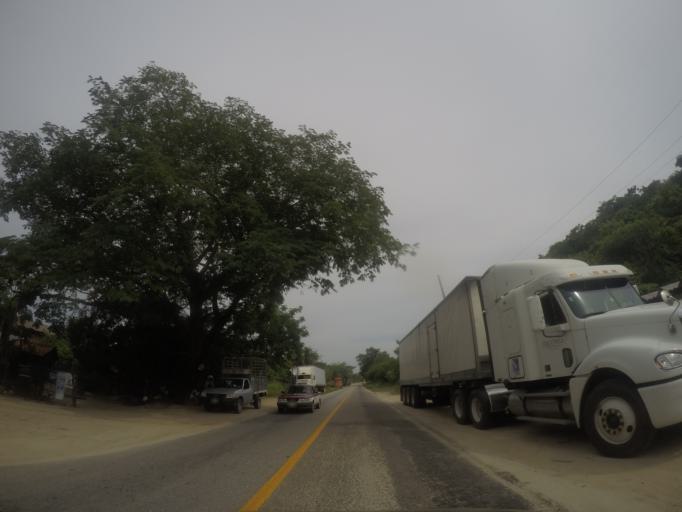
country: MX
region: Oaxaca
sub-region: Villa de Tututepec de Melchor Ocampo
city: Santa Rosa de Lima
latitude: 15.9697
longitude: -97.3972
